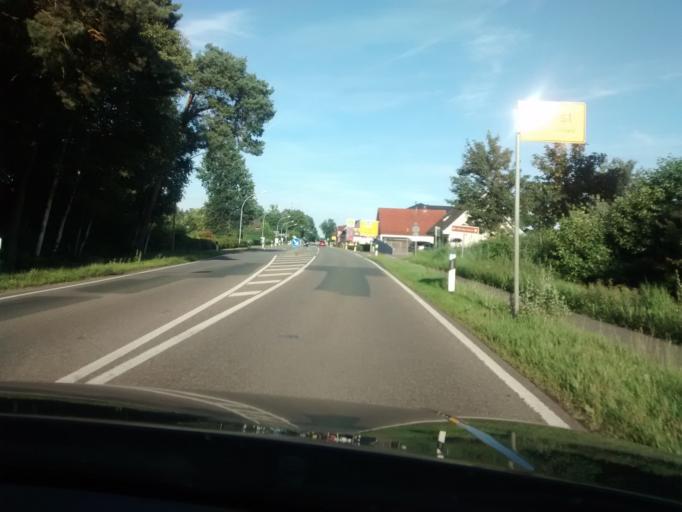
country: DE
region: Lower Saxony
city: Twist
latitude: 52.6493
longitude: 7.0929
